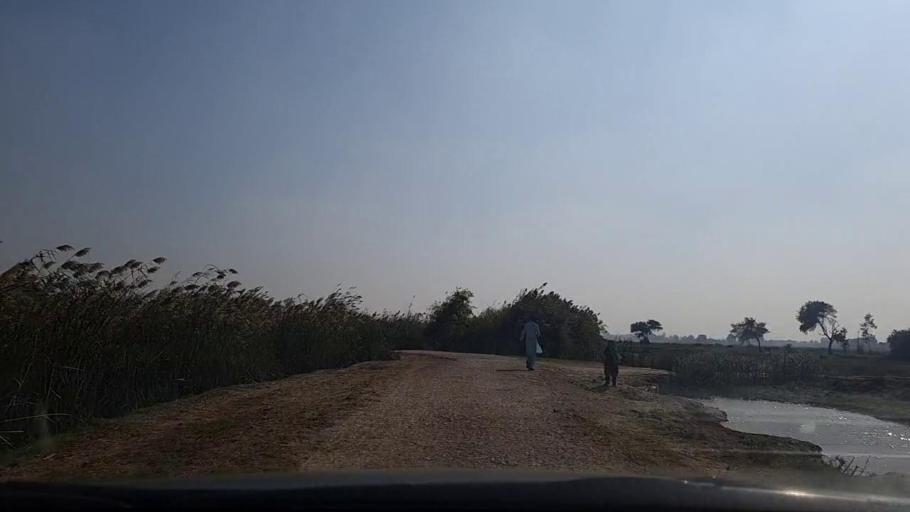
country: PK
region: Sindh
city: Mirpur Sakro
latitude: 24.5506
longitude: 67.6963
